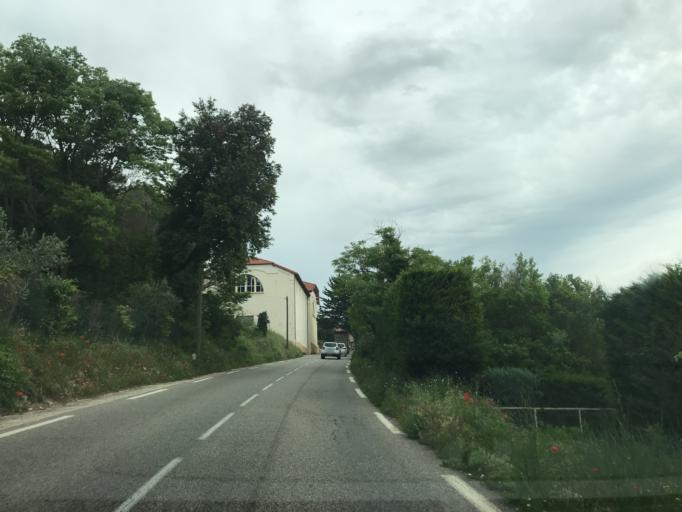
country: FR
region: Provence-Alpes-Cote d'Azur
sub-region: Departement du Var
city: Ginasservis
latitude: 43.6674
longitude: 5.8503
